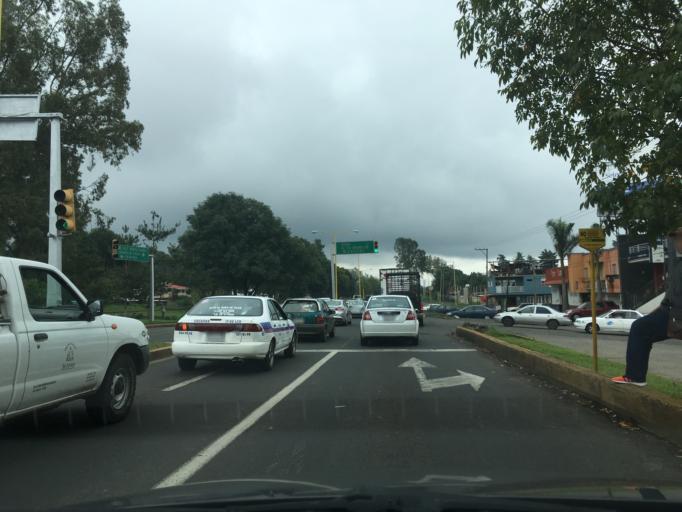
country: MX
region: Michoacan
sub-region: Uruapan
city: Uruapan
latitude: 19.4219
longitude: -102.0366
